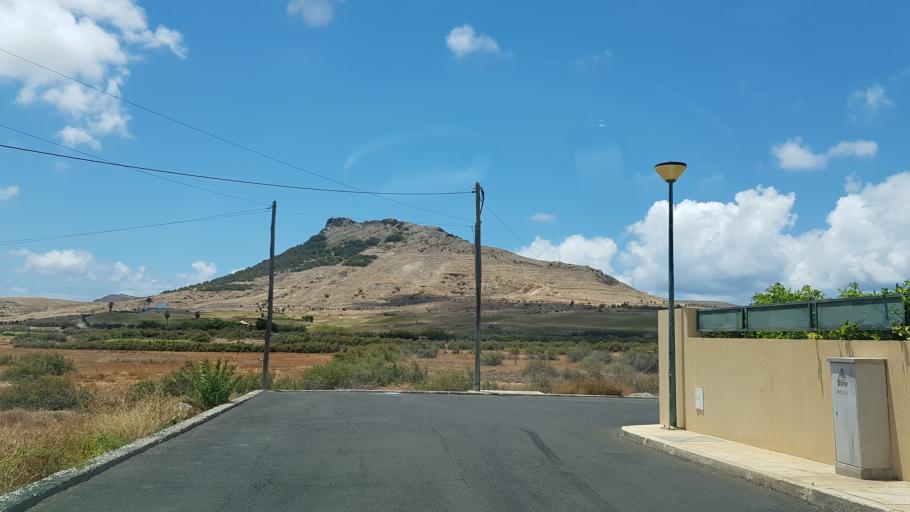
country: PT
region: Madeira
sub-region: Porto Santo
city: Vila de Porto Santo
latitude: 33.0507
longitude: -16.3557
